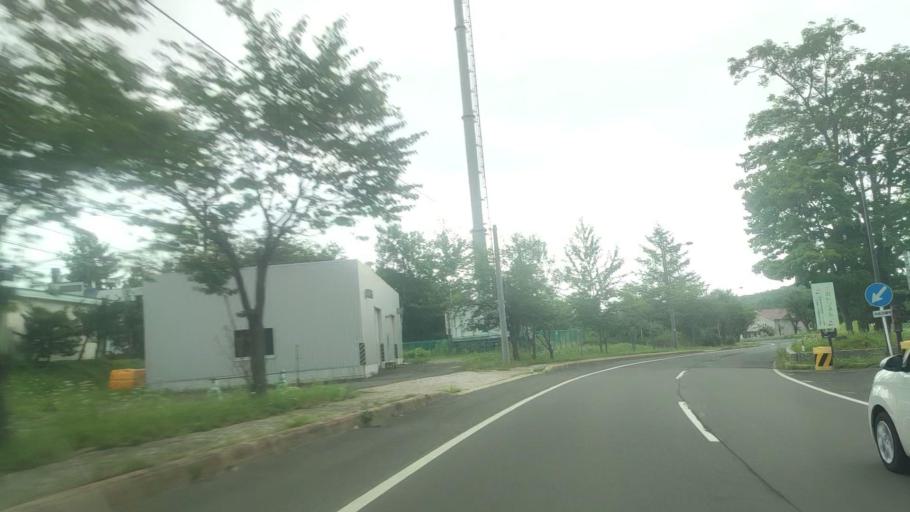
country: JP
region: Hokkaido
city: Shiraoi
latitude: 42.4707
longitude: 141.1596
